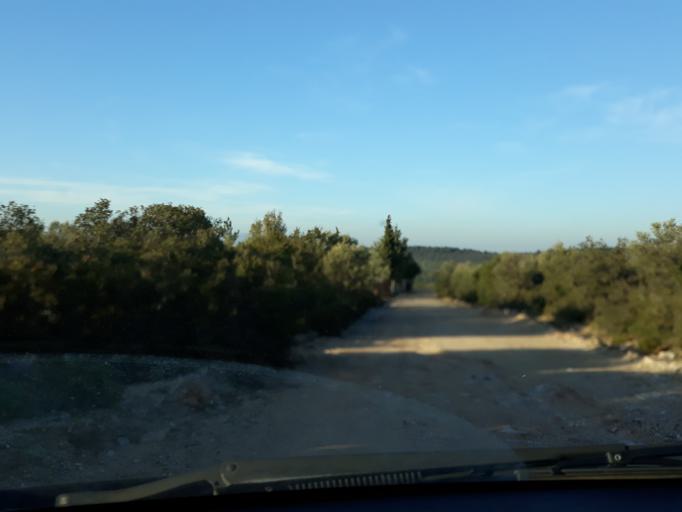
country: GR
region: Central Greece
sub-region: Nomos Voiotias
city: Asopia
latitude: 38.2563
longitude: 23.5345
